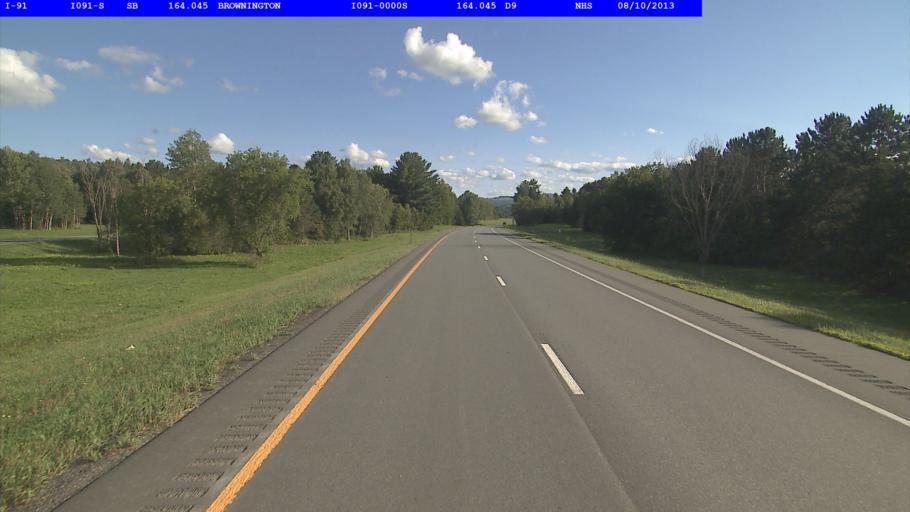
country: US
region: Vermont
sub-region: Orleans County
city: Newport
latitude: 44.8413
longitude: -72.1936
